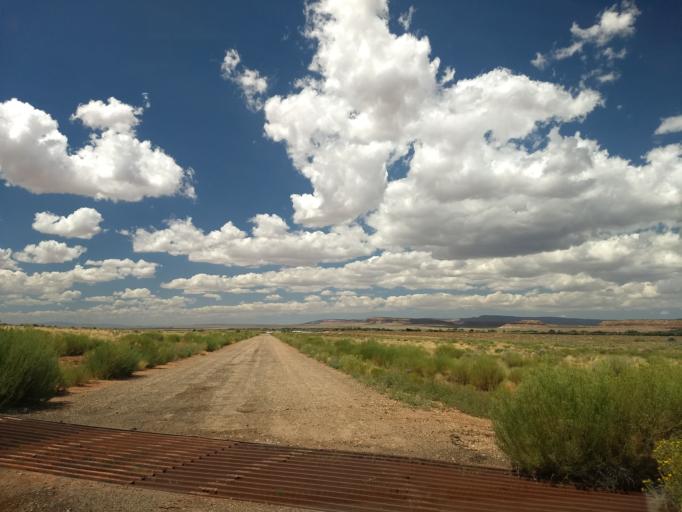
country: US
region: Arizona
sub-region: Coconino County
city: Fredonia
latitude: 36.9448
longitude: -112.5043
